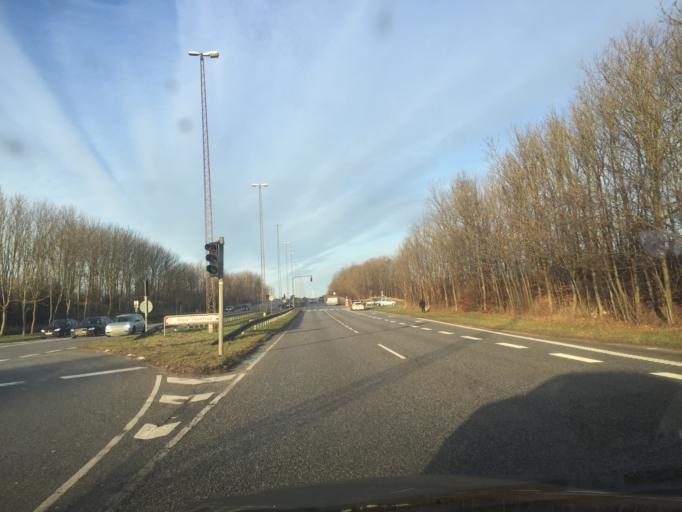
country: DK
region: Capital Region
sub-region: Hoje-Taastrup Kommune
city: Taastrup
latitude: 55.6459
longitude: 12.2818
